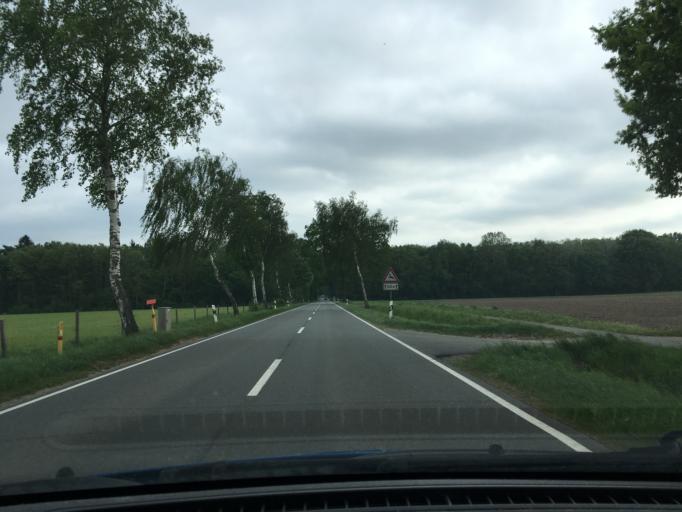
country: DE
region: Lower Saxony
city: Salzhausen
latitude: 53.2078
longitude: 10.1909
